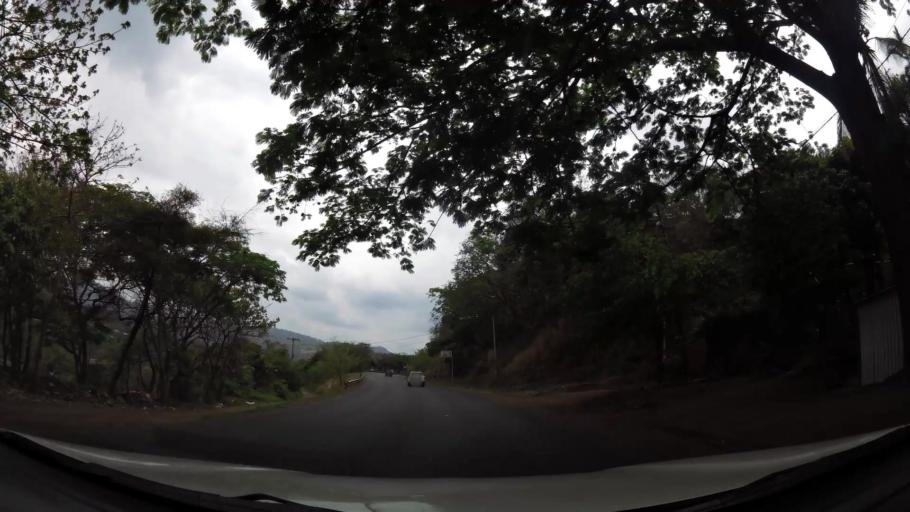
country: NI
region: Matagalpa
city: Matagalpa
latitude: 12.9126
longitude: -85.9464
